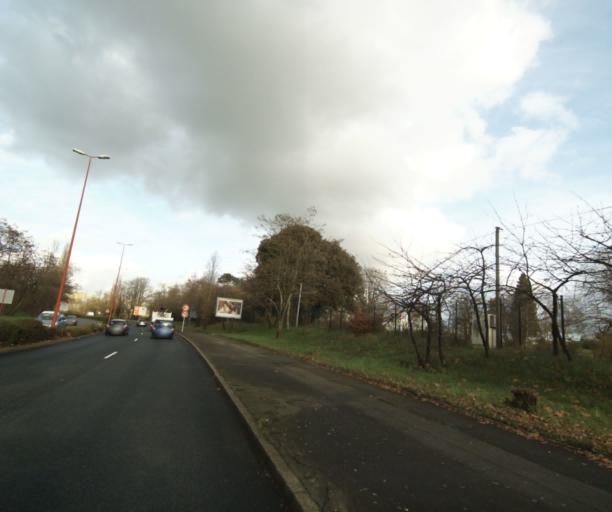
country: FR
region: Pays de la Loire
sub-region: Departement de la Sarthe
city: Le Mans
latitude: 47.9865
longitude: 0.2260
